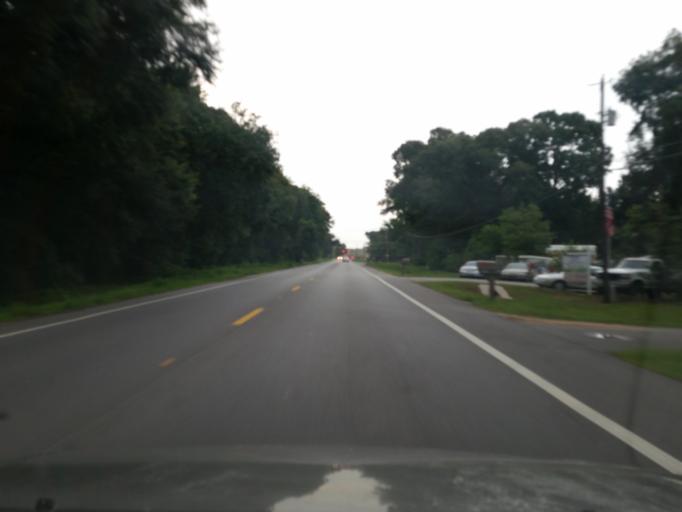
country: US
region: Florida
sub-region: Escambia County
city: Ensley
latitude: 30.5380
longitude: -87.3181
